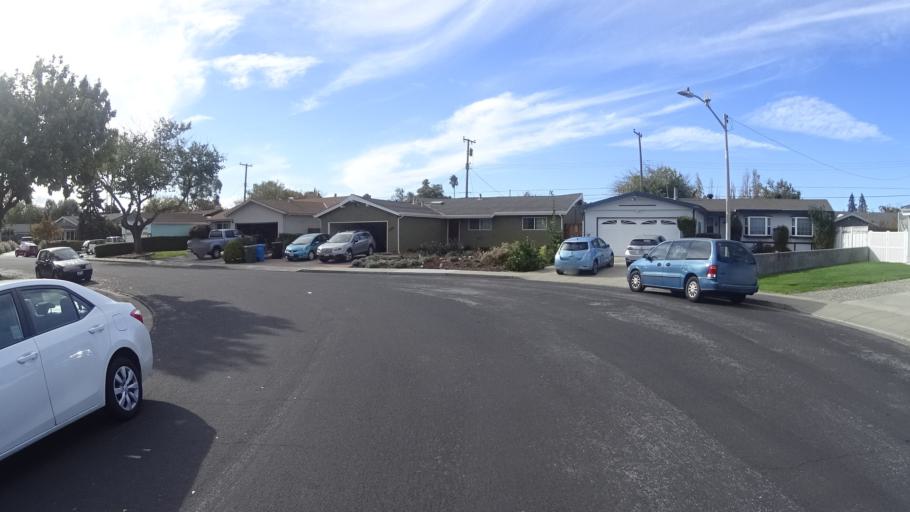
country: US
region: California
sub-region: Santa Clara County
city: Santa Clara
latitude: 37.3610
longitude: -121.9665
